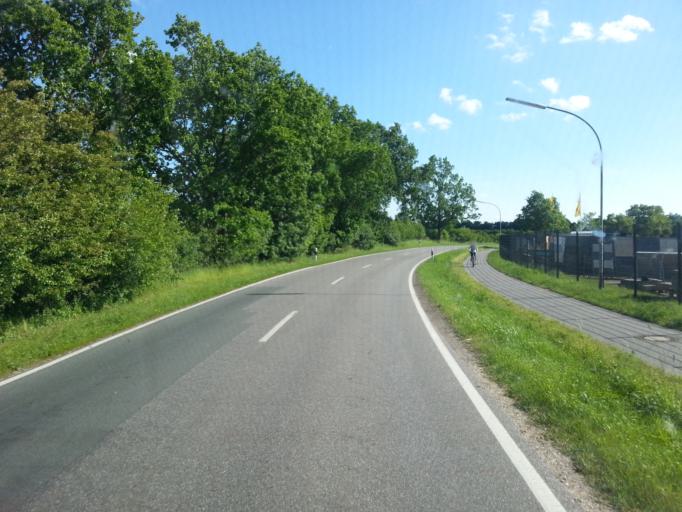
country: DE
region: Schleswig-Holstein
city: Ratekau
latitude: 53.9960
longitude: 10.7178
